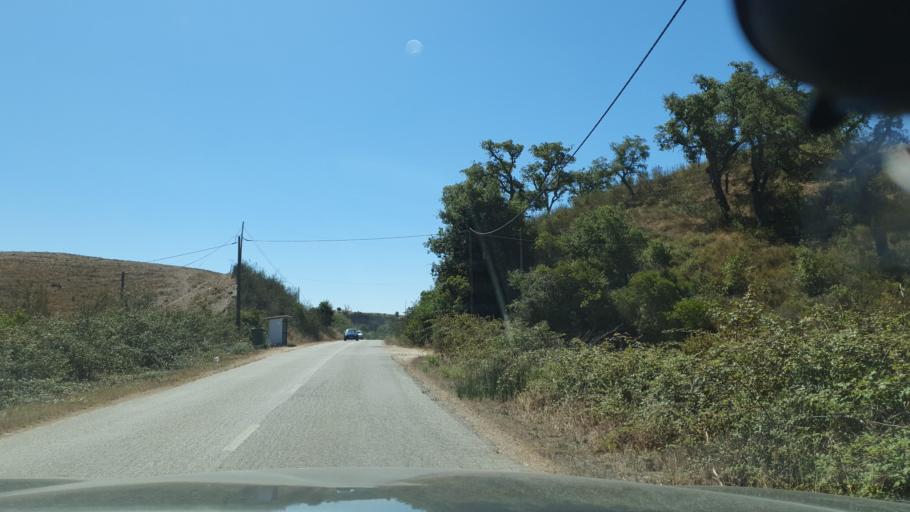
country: PT
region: Beja
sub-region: Odemira
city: Sao Teotonio
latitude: 37.4943
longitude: -8.6442
